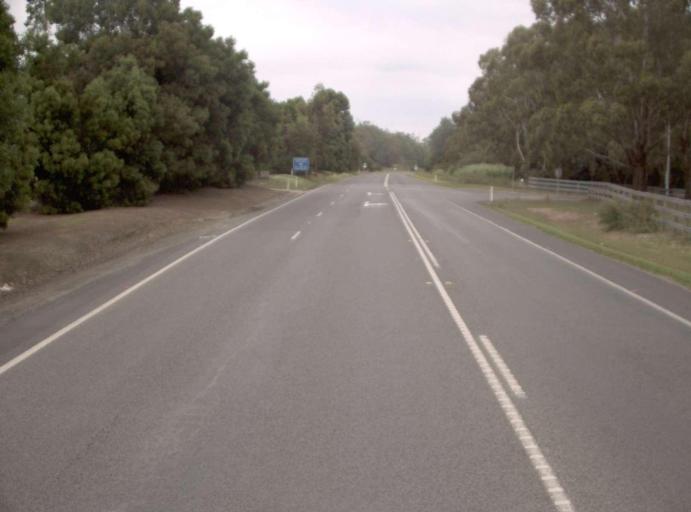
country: AU
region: Victoria
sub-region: Bass Coast
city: North Wonthaggi
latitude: -38.5348
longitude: 145.9505
